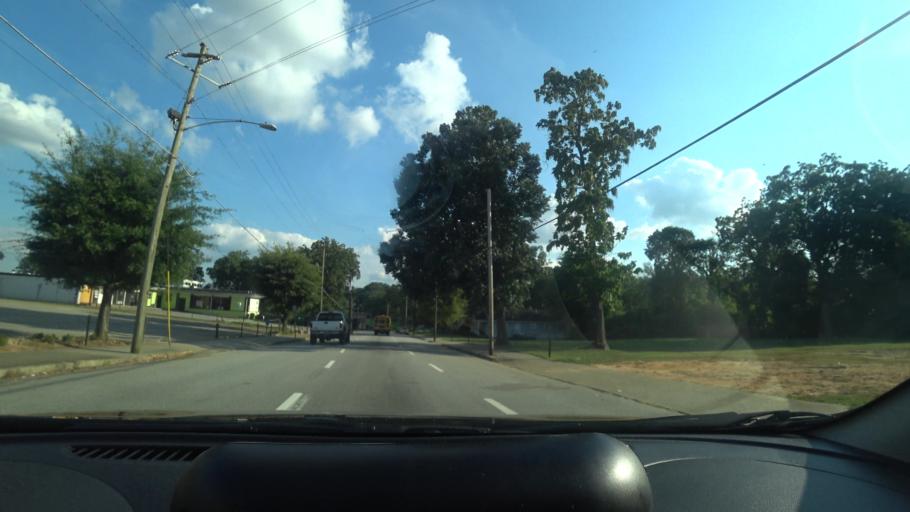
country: US
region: Georgia
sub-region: Fulton County
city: Atlanta
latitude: 33.7356
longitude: -84.3945
